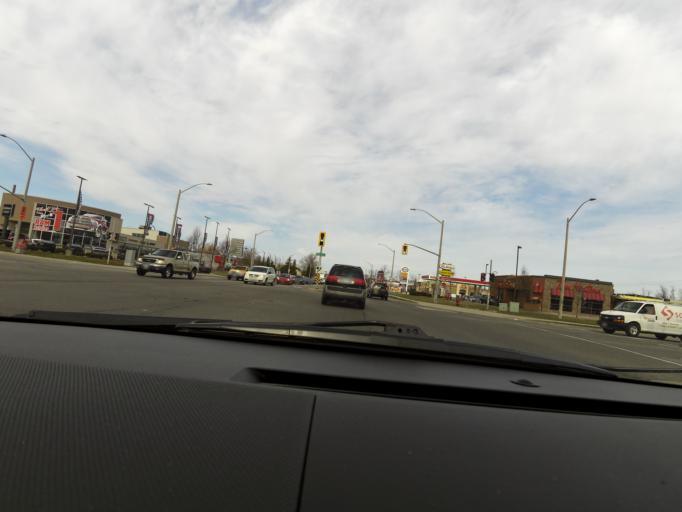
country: CA
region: Ontario
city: Hamilton
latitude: 43.2110
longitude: -79.8892
